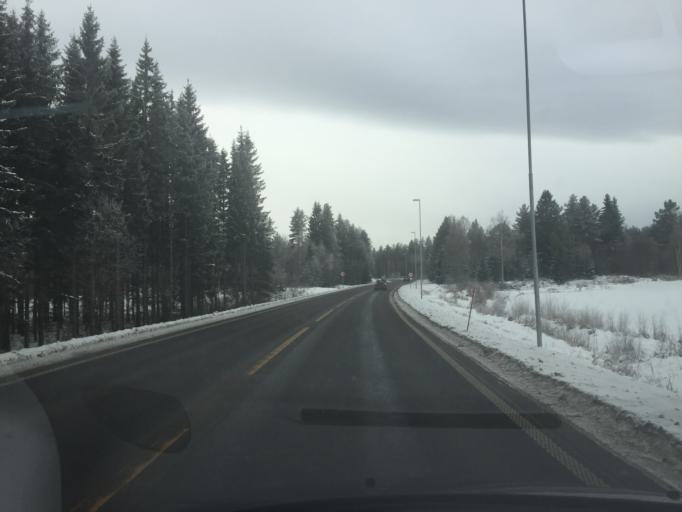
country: NO
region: Hedmark
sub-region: Elverum
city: Elverum
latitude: 60.9060
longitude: 11.6109
